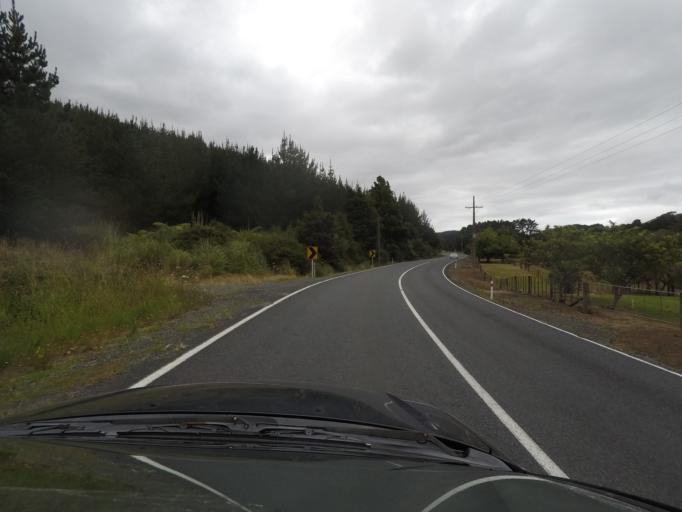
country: NZ
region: Auckland
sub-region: Auckland
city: Wellsford
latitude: -36.2925
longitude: 174.6146
